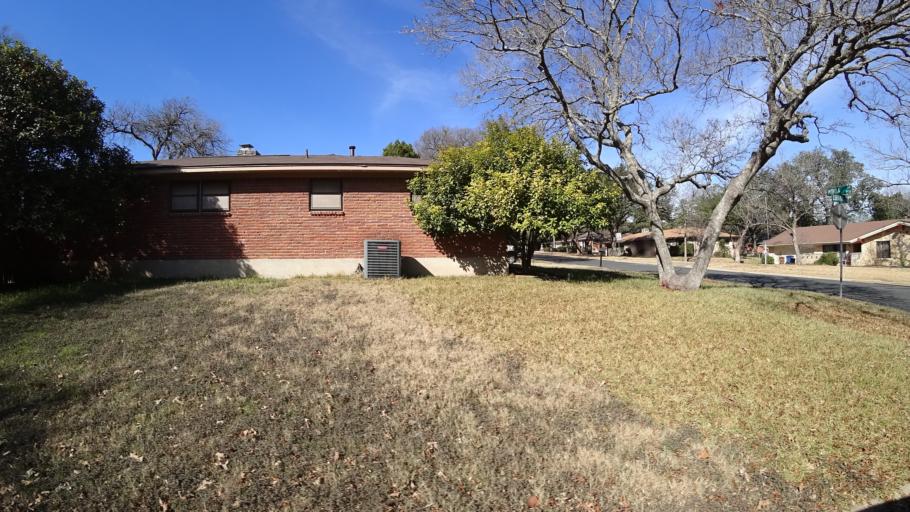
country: US
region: Texas
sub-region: Travis County
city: Wells Branch
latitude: 30.3869
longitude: -97.6875
